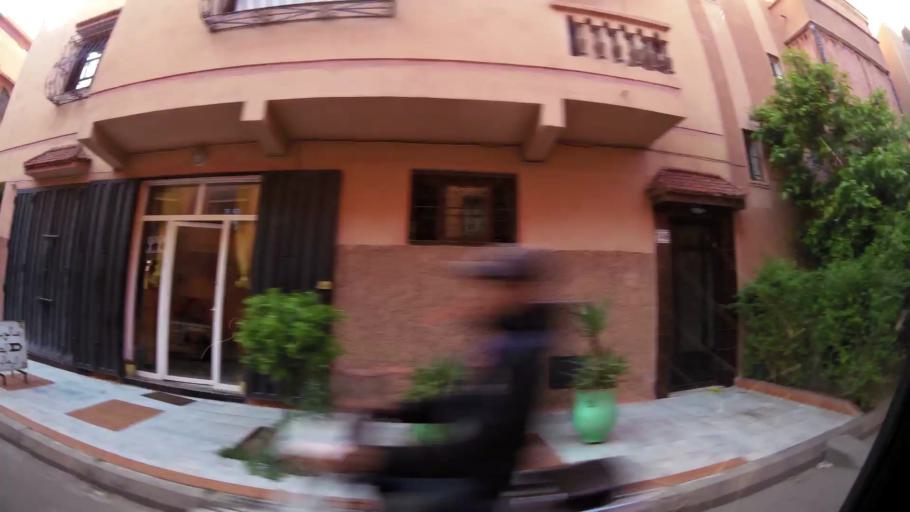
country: MA
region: Marrakech-Tensift-Al Haouz
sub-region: Marrakech
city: Marrakesh
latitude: 31.6220
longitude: -8.0687
